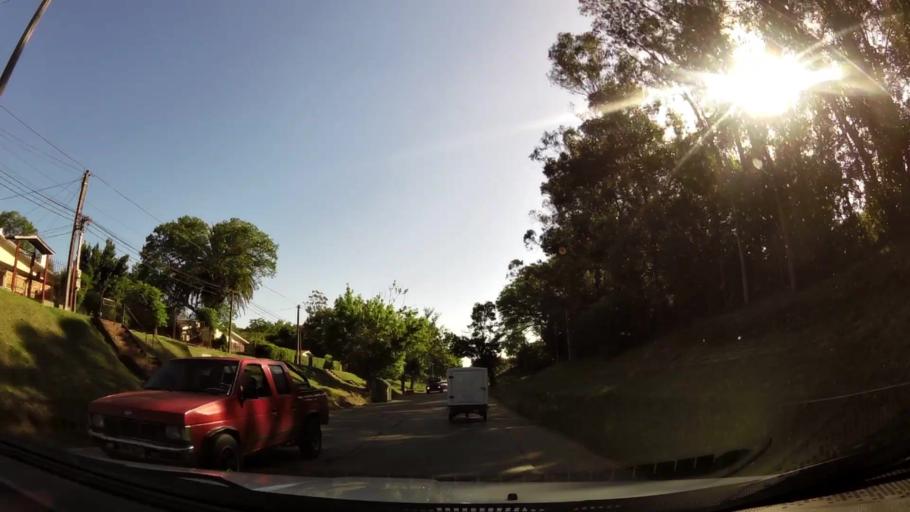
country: UY
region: Canelones
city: La Paz
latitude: -34.8237
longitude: -56.1796
